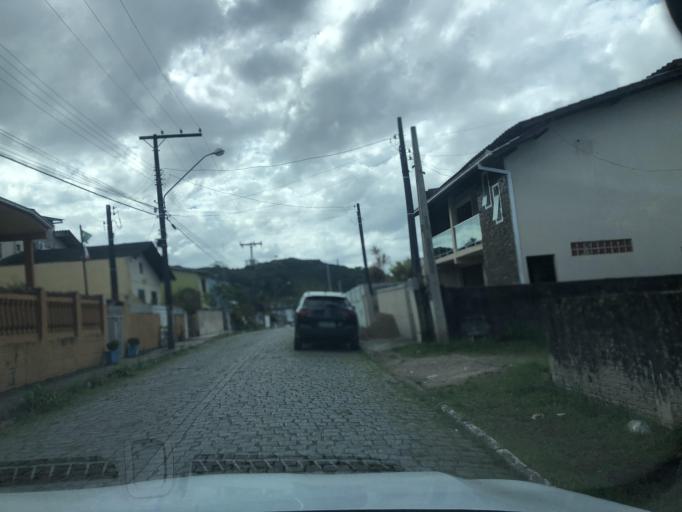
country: BR
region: Santa Catarina
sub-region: Sao Francisco Do Sul
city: Sao Francisco do Sul
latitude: -26.2474
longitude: -48.6299
